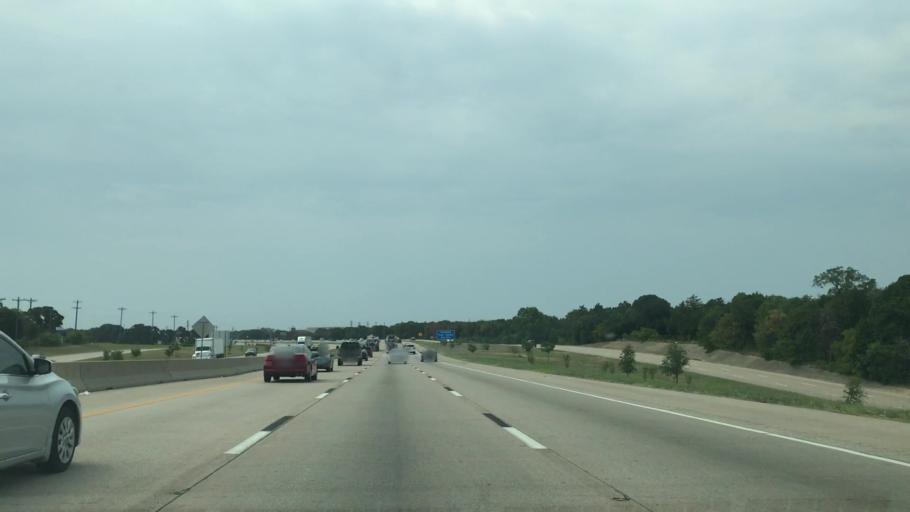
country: US
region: Texas
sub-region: Tarrant County
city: Southlake
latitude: 32.9687
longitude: -97.1582
